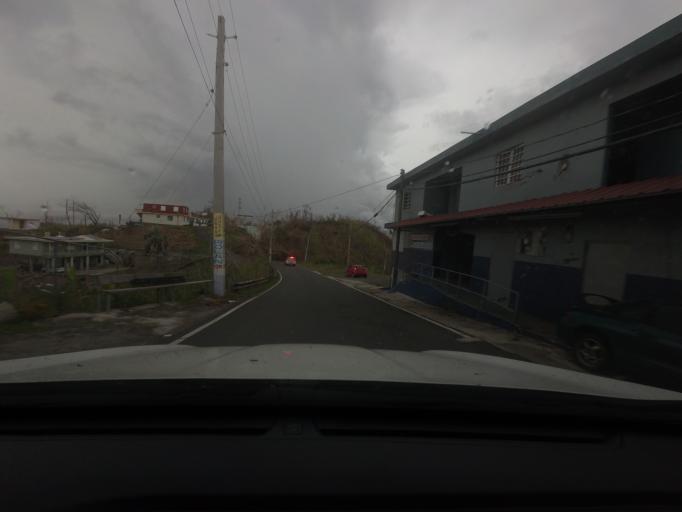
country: PR
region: Ciales
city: Ciales
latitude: 18.2740
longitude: -66.4805
